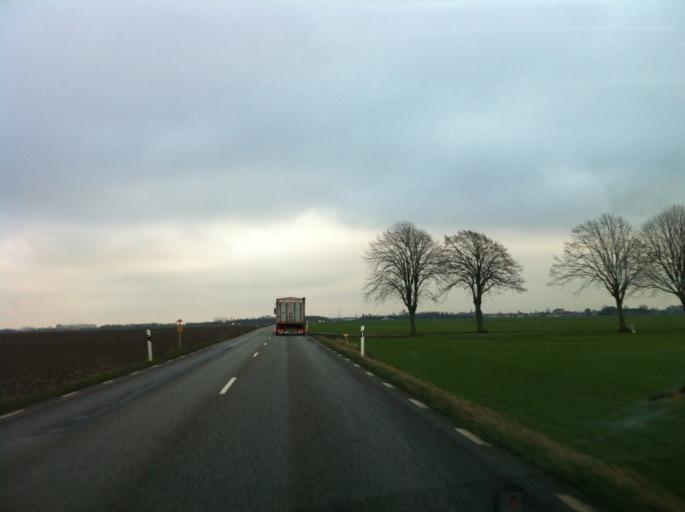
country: SE
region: Skane
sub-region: Kavlinge Kommun
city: Kaevlinge
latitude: 55.8044
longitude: 13.0809
